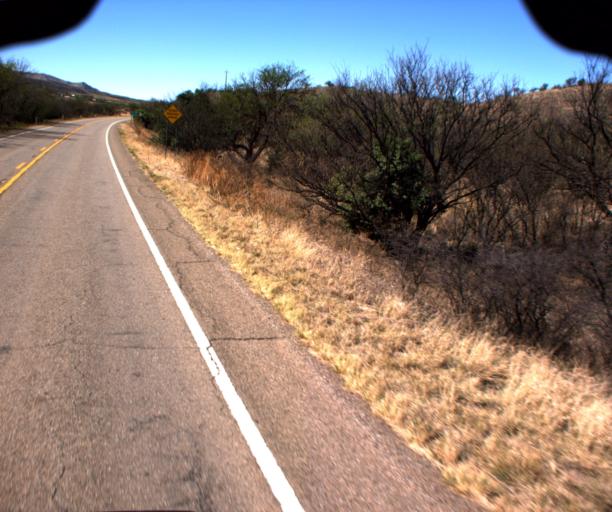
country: US
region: Arizona
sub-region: Santa Cruz County
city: Rio Rico
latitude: 31.5520
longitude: -110.7380
